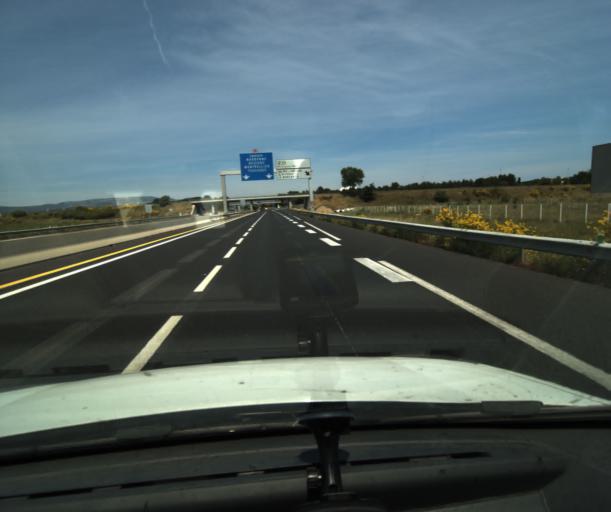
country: FR
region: Languedoc-Roussillon
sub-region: Departement des Pyrenees-Orientales
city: Rivesaltes
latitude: 42.7799
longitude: 2.8947
